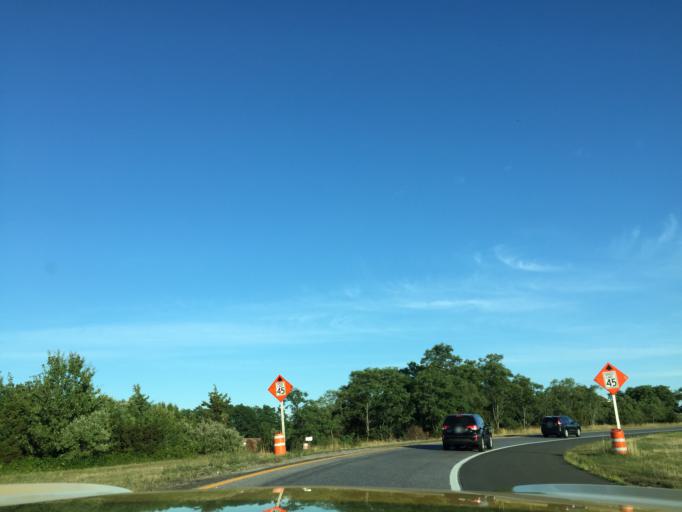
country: US
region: New York
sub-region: Suffolk County
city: Calverton
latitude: 40.9245
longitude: -72.7190
